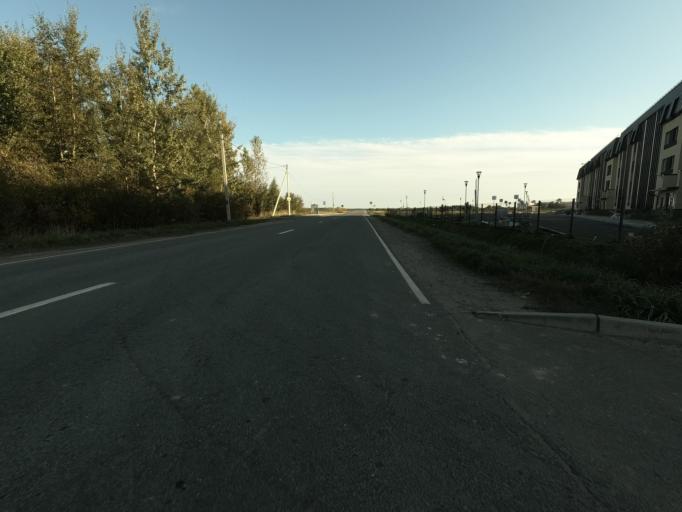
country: RU
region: St.-Petersburg
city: Pontonnyy
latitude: 59.7554
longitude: 30.6314
